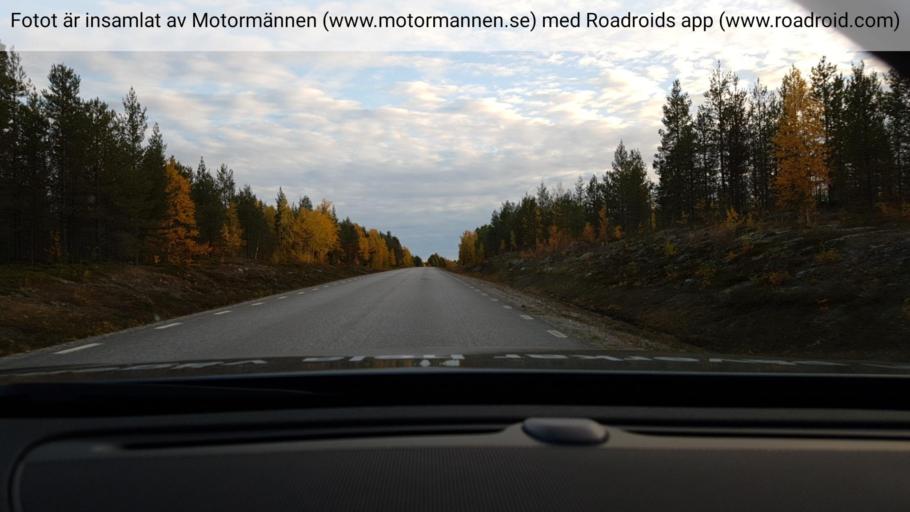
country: SE
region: Norrbotten
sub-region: Jokkmokks Kommun
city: Jokkmokk
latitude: 66.4411
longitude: 19.6926
